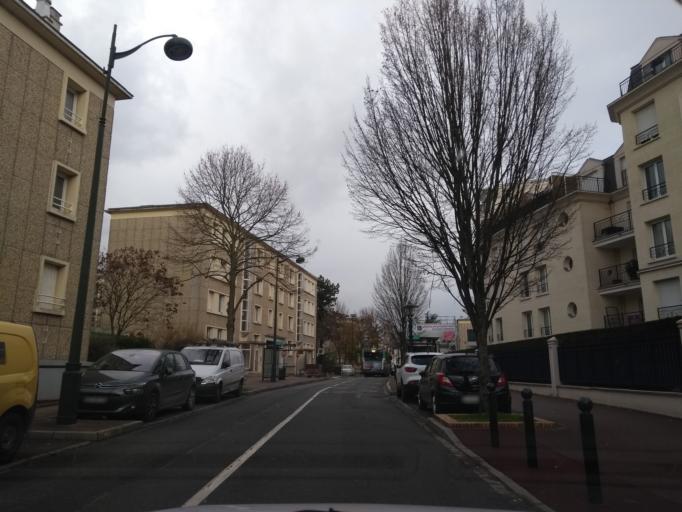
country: FR
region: Ile-de-France
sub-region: Departement des Hauts-de-Seine
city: Chatenay-Malabry
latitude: 48.7739
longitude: 2.2572
